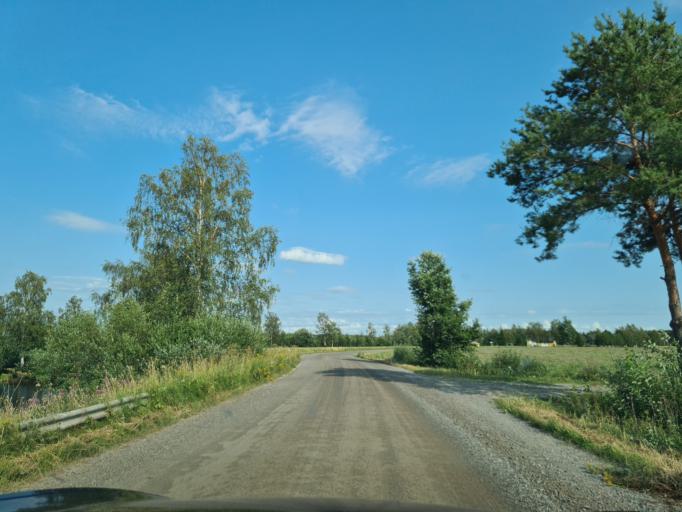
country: FI
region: Ostrobothnia
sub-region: Kyroenmaa
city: Laihia
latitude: 63.0302
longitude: 21.8911
